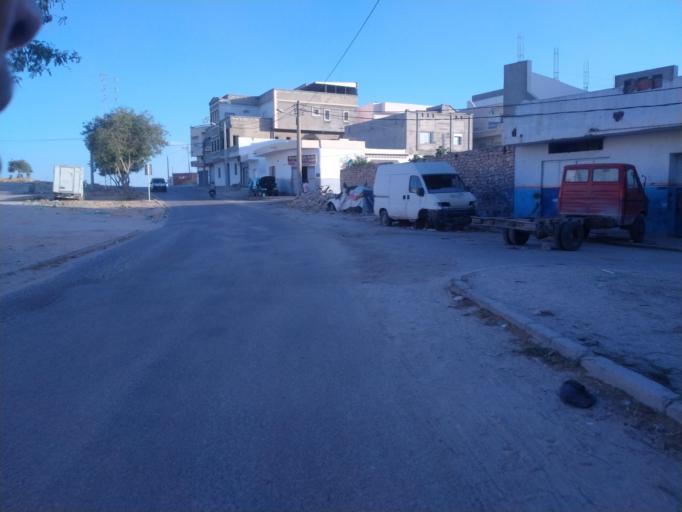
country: TN
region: Susah
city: Akouda
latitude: 35.8170
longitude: 10.5536
